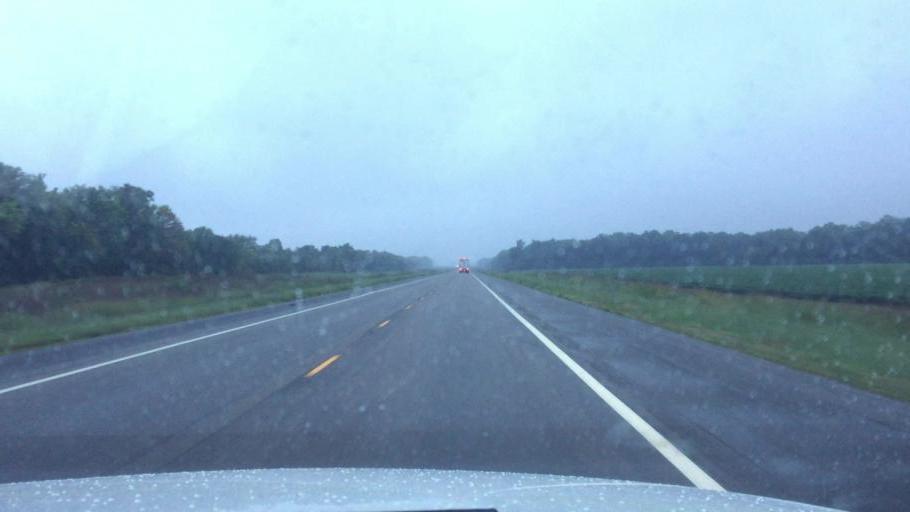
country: US
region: Kansas
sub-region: Montgomery County
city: Cherryvale
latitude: 37.4211
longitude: -95.4945
